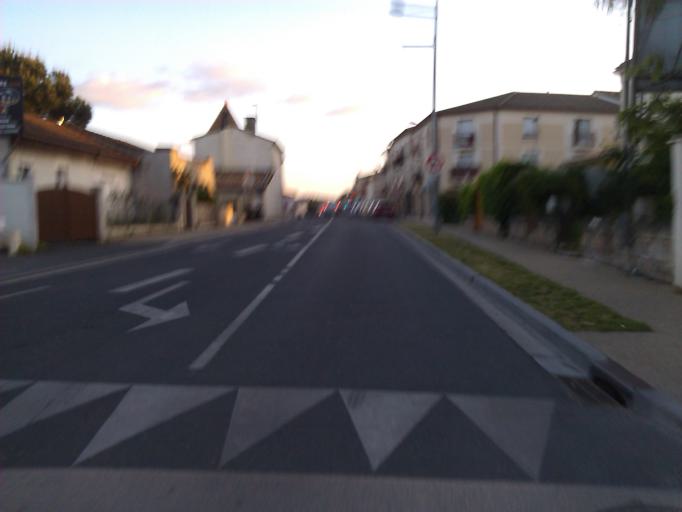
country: FR
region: Aquitaine
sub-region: Departement de la Gironde
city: Carbon-Blanc
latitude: 44.8971
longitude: -0.4977
